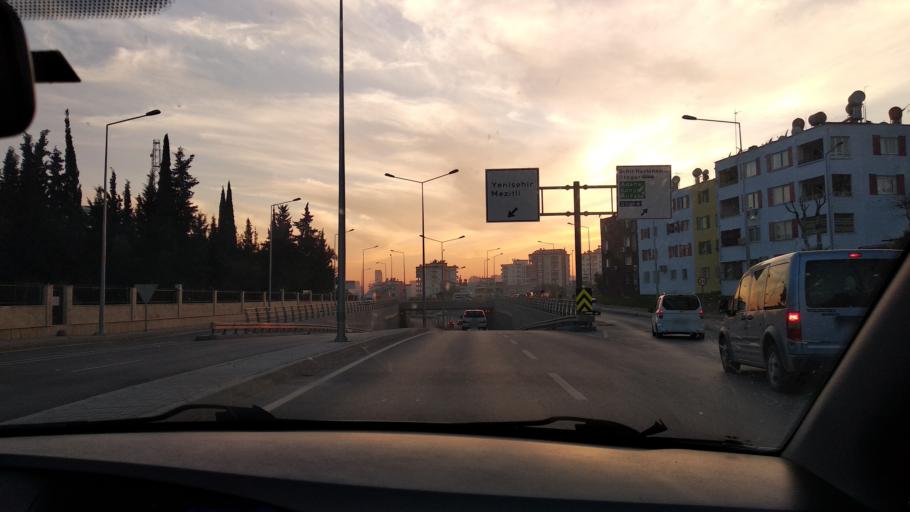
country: TR
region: Mersin
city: Mercin
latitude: 36.8211
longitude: 34.5990
